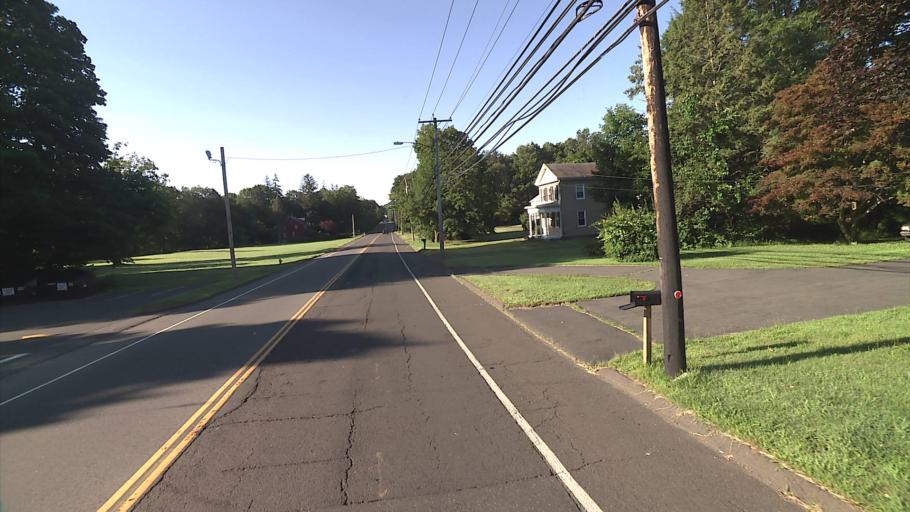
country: US
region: Connecticut
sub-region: New Haven County
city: Hamden
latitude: 41.4281
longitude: -72.9063
